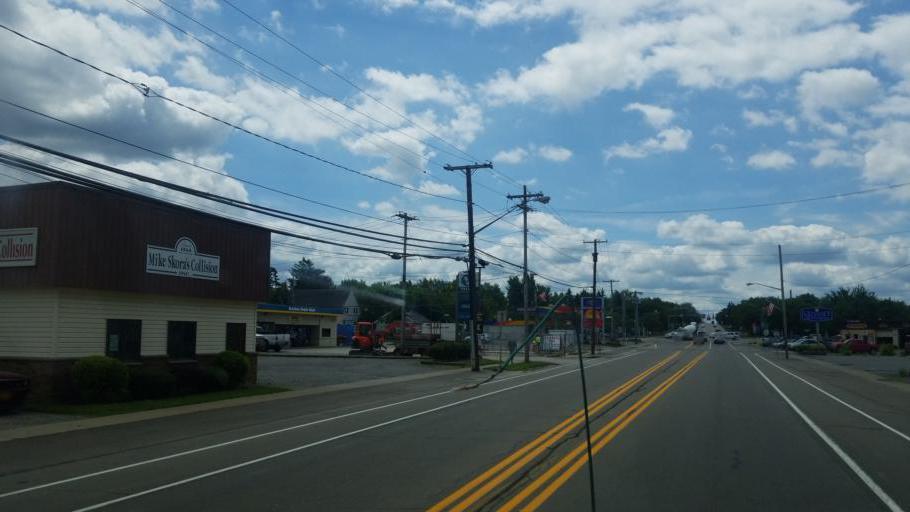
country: US
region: New York
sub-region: Erie County
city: Blasdell
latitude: 42.7909
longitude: -78.8239
